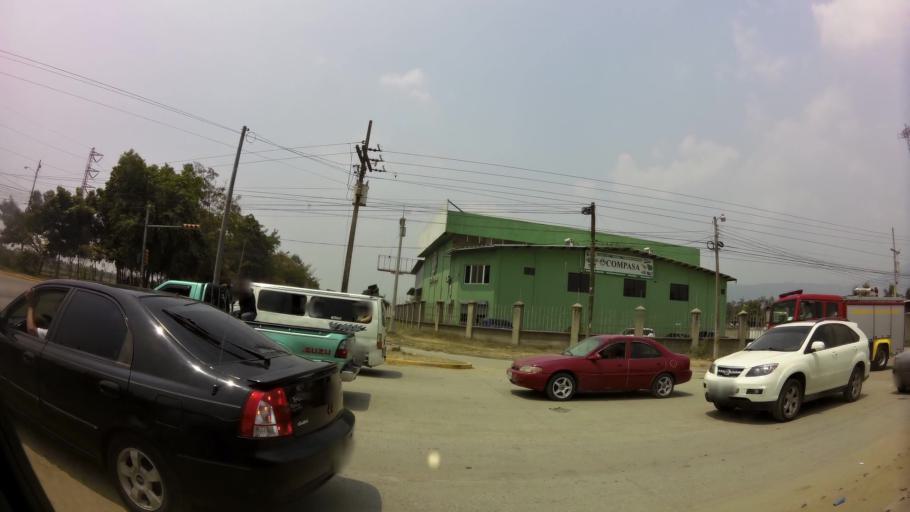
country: HN
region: Cortes
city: San Pedro Sula
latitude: 15.4790
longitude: -88.0078
